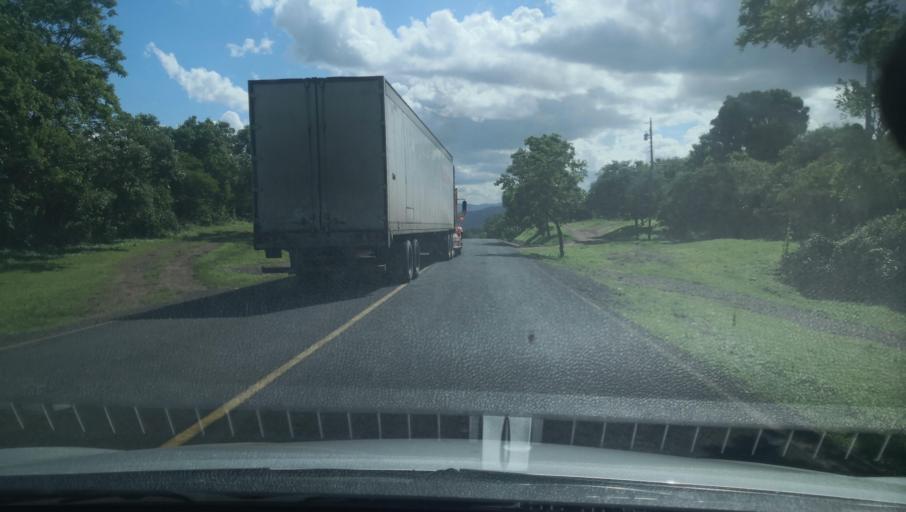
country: NI
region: Madriz
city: Somoto
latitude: 13.4723
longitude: -86.6165
